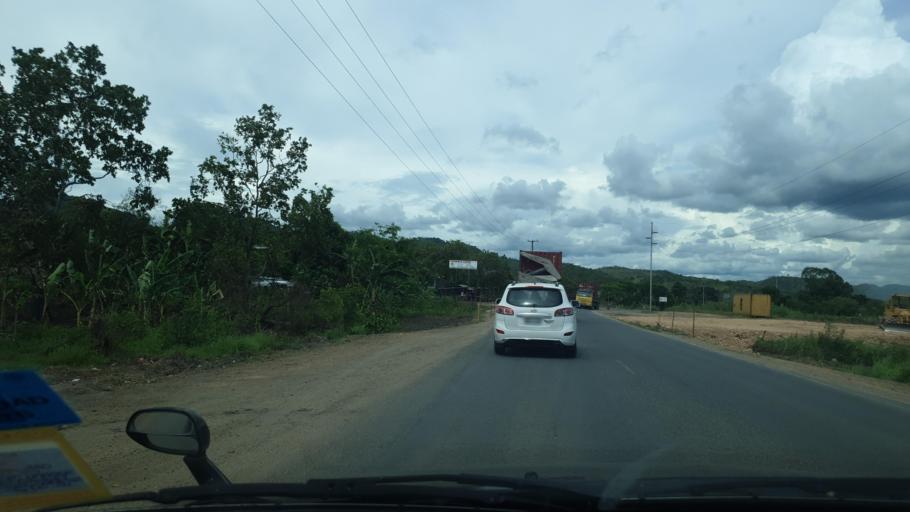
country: PG
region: National Capital
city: Port Moresby
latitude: -9.4169
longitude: 147.1075
